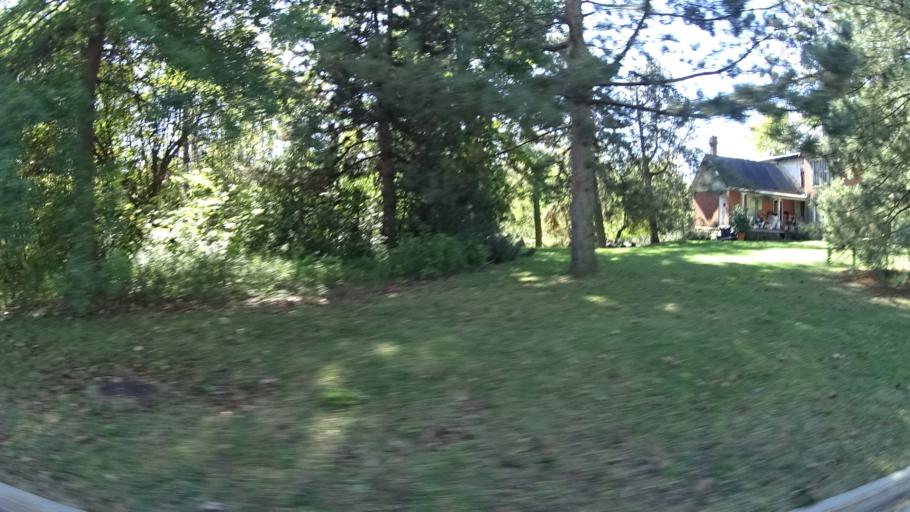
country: US
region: Ohio
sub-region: Lorain County
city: Oberlin
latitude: 41.2914
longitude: -82.1980
